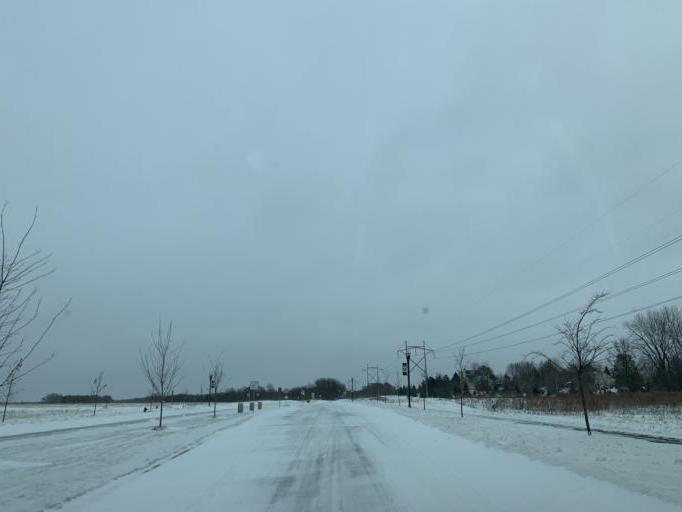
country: US
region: Minnesota
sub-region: Washington County
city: Cottage Grove
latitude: 44.8559
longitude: -92.9081
